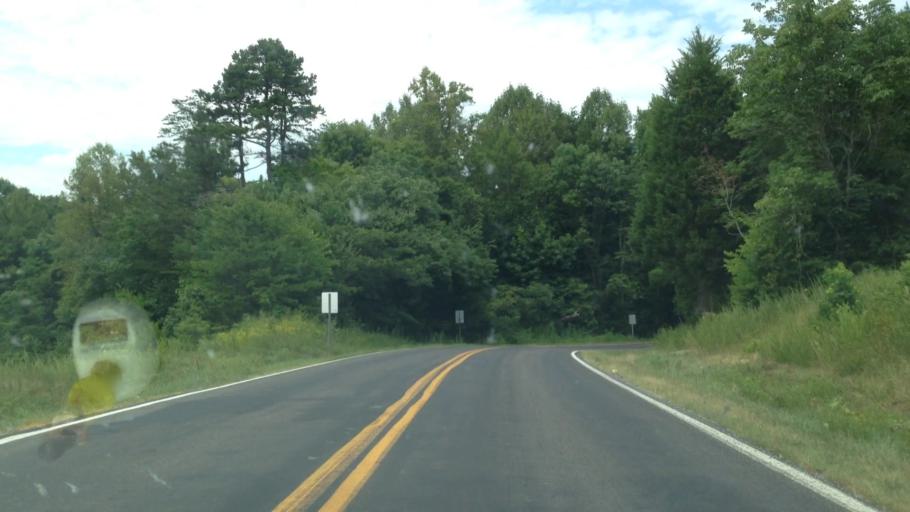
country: US
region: North Carolina
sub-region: Stokes County
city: Walnut Cove
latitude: 36.2523
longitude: -80.0990
